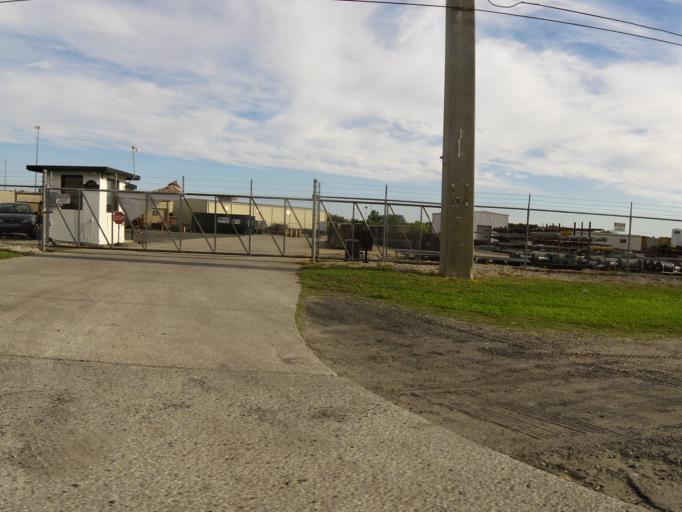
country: US
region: Florida
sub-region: Duval County
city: Jacksonville
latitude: 30.3334
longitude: -81.6801
